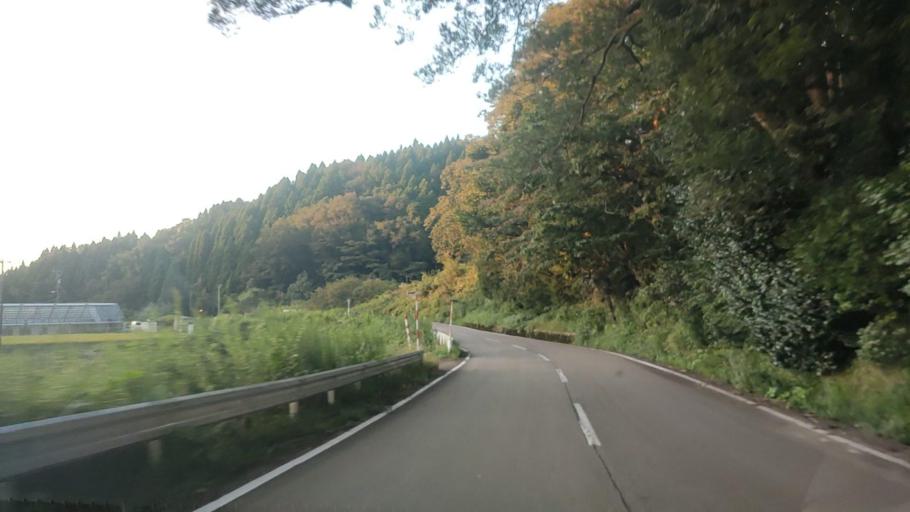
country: JP
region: Ishikawa
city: Tsubata
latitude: 36.6251
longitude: 136.7787
